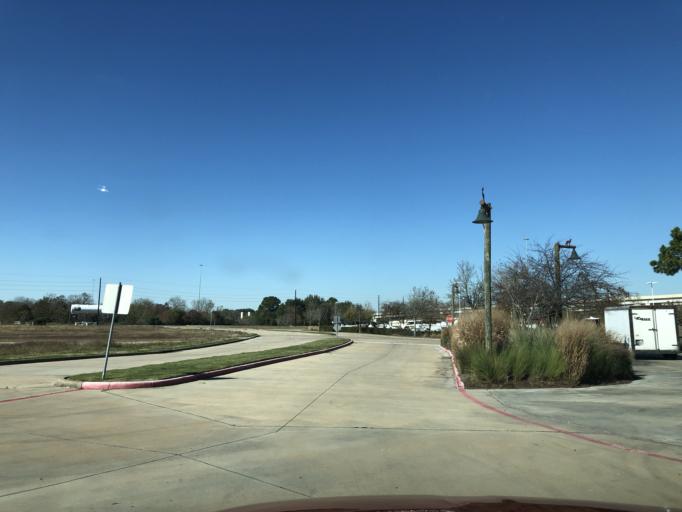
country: US
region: Texas
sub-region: Brazoria County
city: Brookside Village
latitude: 29.5946
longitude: -95.3903
